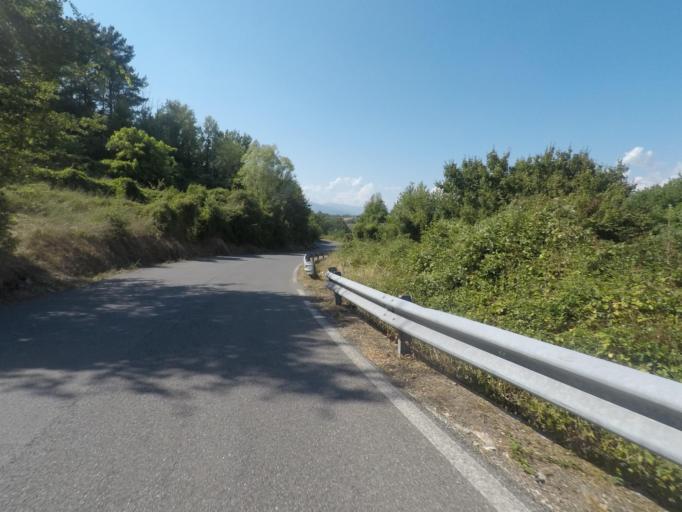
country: IT
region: Tuscany
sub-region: Provincia di Massa-Carrara
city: Pallerone
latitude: 44.1960
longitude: 10.0542
